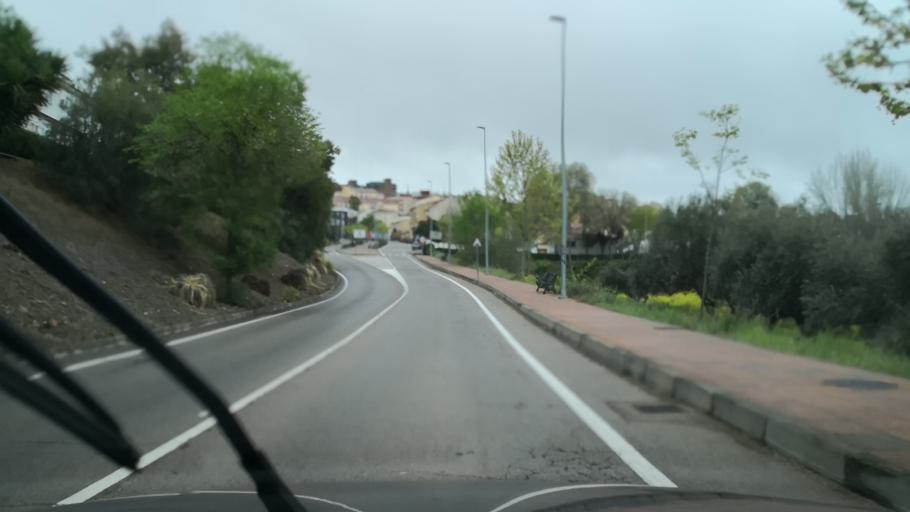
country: ES
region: Extremadura
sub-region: Provincia de Caceres
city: Caceres
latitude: 39.4824
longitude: -6.3802
